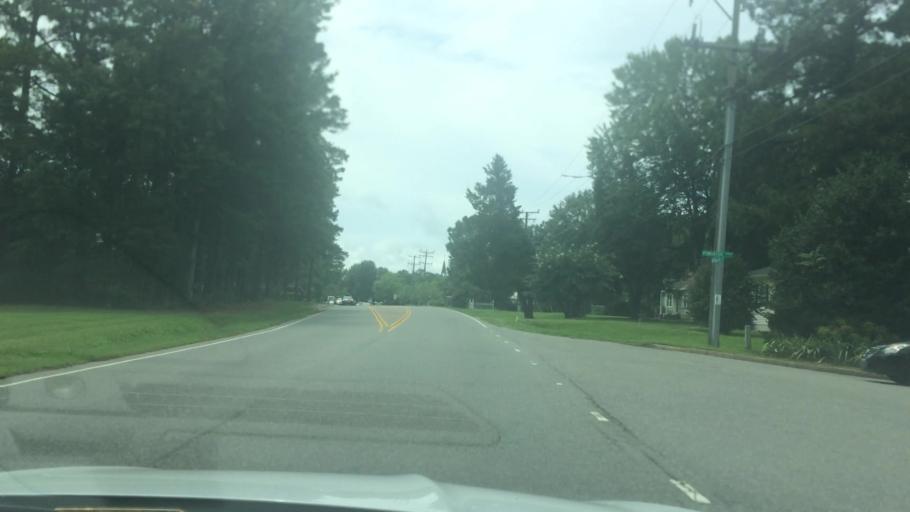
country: US
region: Virginia
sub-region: James City County
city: Williamsburg
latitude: 37.2558
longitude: -76.7657
